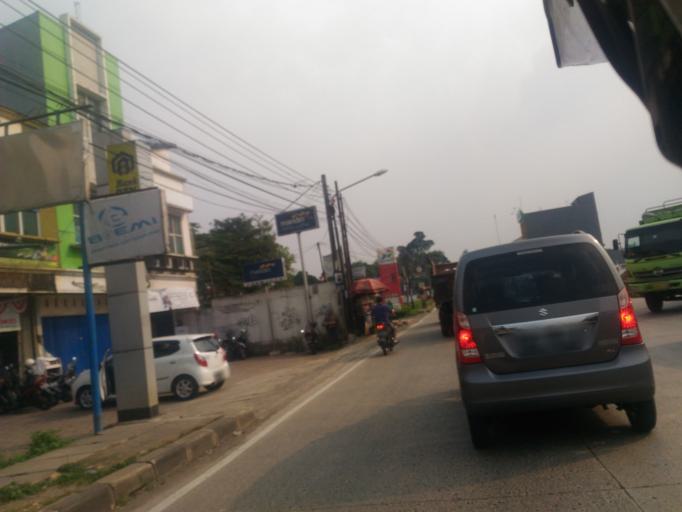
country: ID
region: West Java
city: Caringin
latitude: -6.6592
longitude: 106.8456
